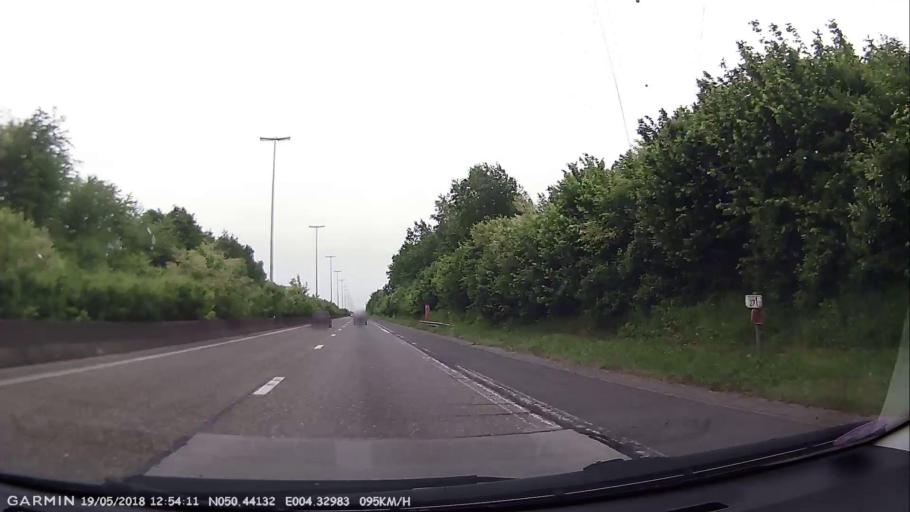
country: BE
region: Wallonia
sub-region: Province du Hainaut
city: Courcelles
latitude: 50.4415
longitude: 4.3296
